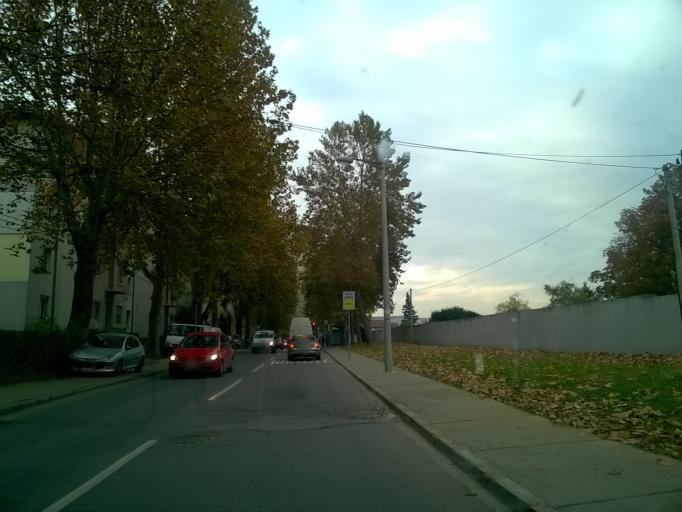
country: RS
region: Central Serbia
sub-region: Belgrade
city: Palilula
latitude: 44.8070
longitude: 20.4939
